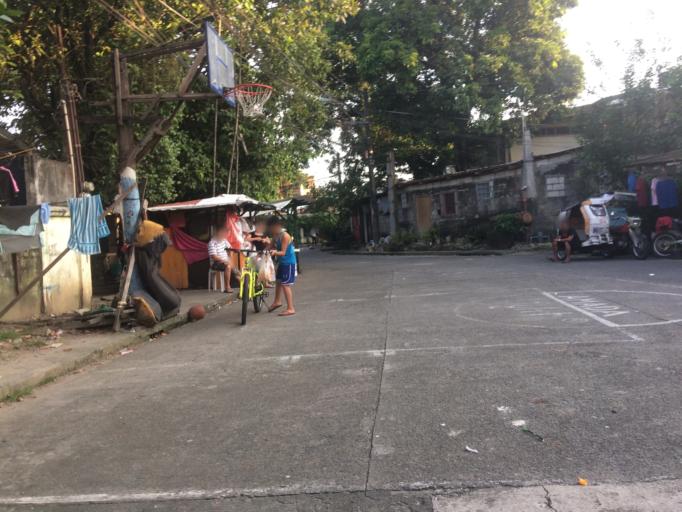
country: PH
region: Calabarzon
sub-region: Province of Rizal
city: Cainta
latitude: 14.5927
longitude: 121.1045
